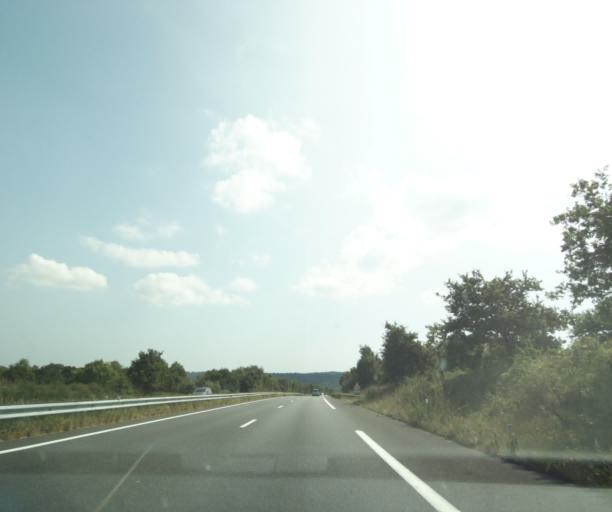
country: FR
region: Brittany
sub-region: Departement du Finistere
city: Hopital-Camfrout
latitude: 48.3498
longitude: -4.2353
